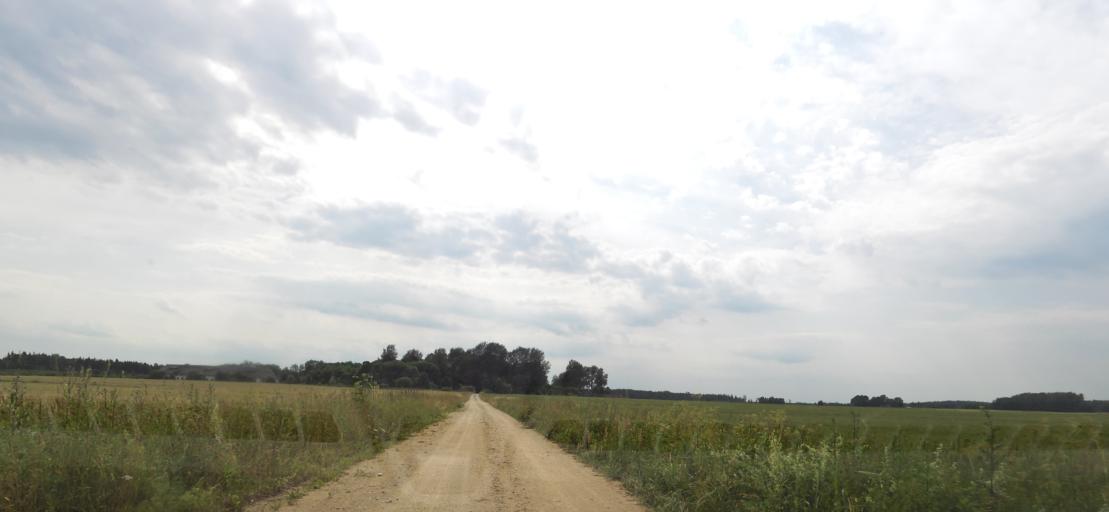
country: LT
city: Obeliai
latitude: 56.1848
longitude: 25.0494
